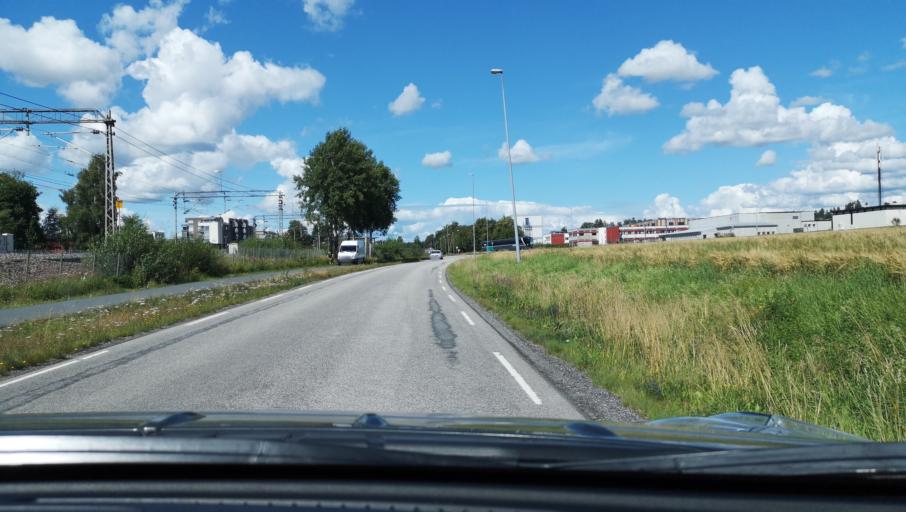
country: NO
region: Akershus
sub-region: As
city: As
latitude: 59.6599
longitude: 10.7968
